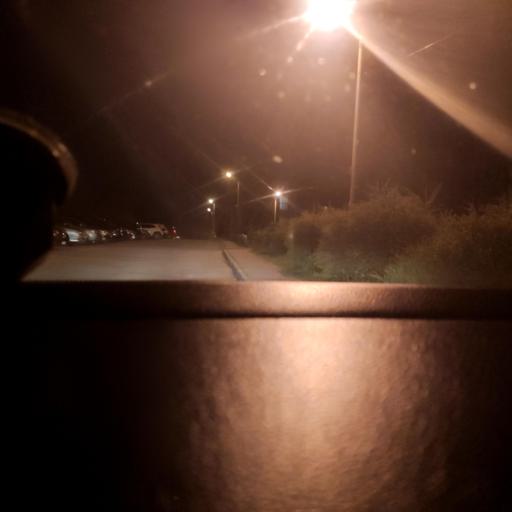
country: RU
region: Moskovskaya
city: Tomilino
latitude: 55.6558
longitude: 37.9678
